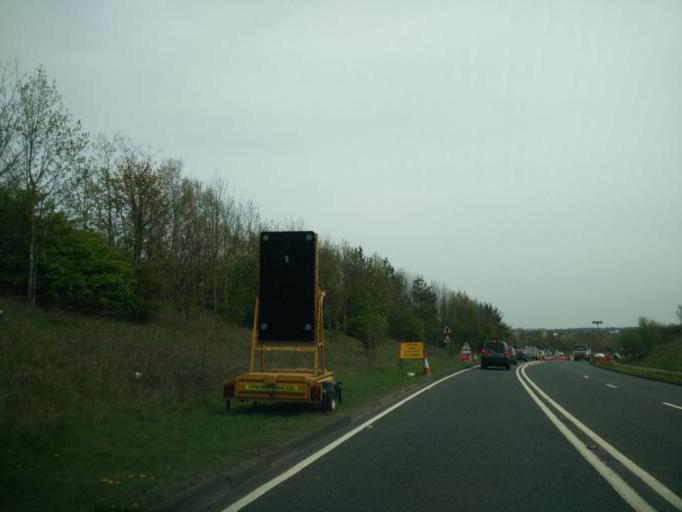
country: GB
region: England
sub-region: County Durham
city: Bishop Auckland
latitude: 54.6706
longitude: -1.6854
